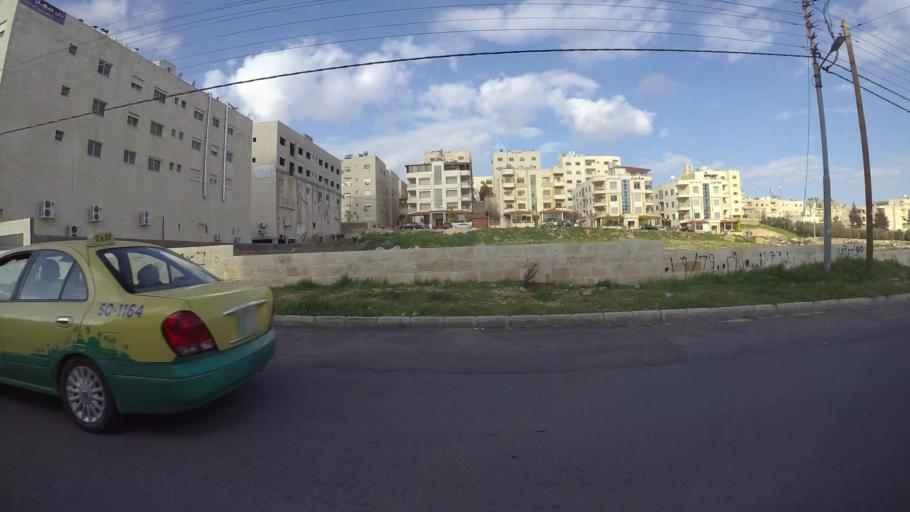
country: JO
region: Amman
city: Al Jubayhah
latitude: 31.9856
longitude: 35.8551
